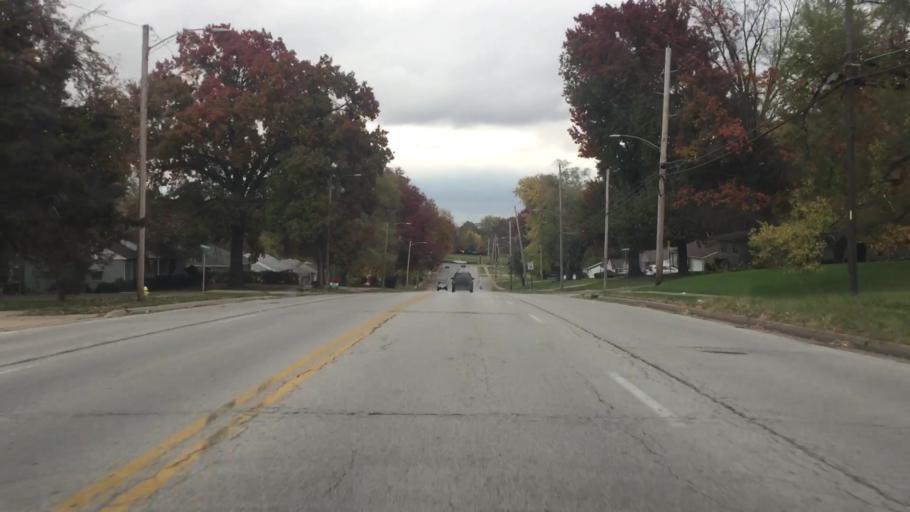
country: US
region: Missouri
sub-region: Jackson County
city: Raytown
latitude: 38.9945
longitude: -94.4685
